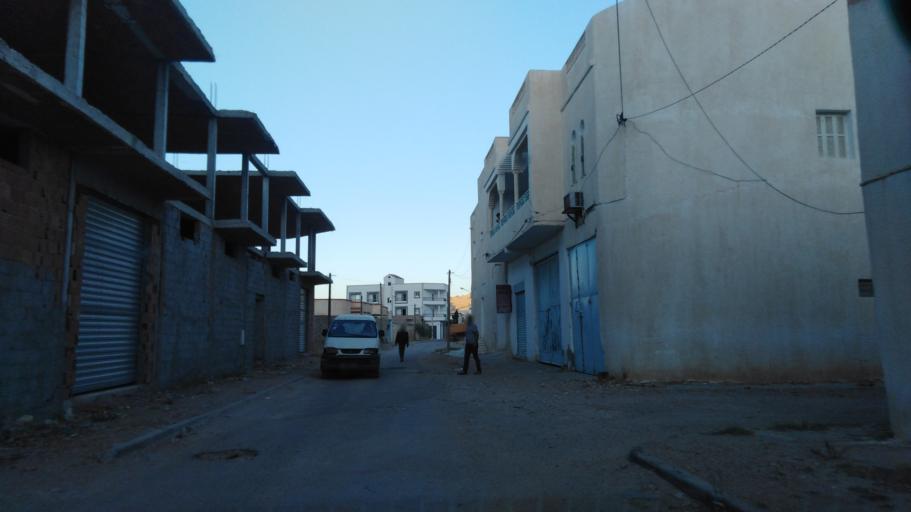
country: TN
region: Tataouine
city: Tataouine
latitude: 32.9422
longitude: 10.4530
